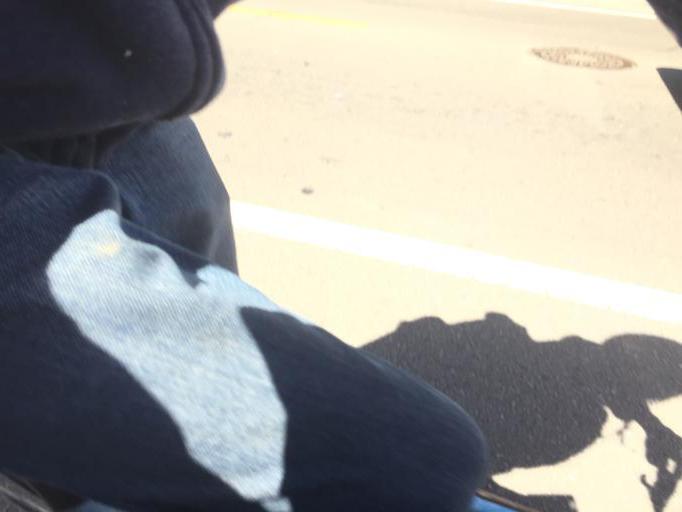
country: US
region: California
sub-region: San Francisco County
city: San Francisco
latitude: 37.8056
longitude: -122.4213
